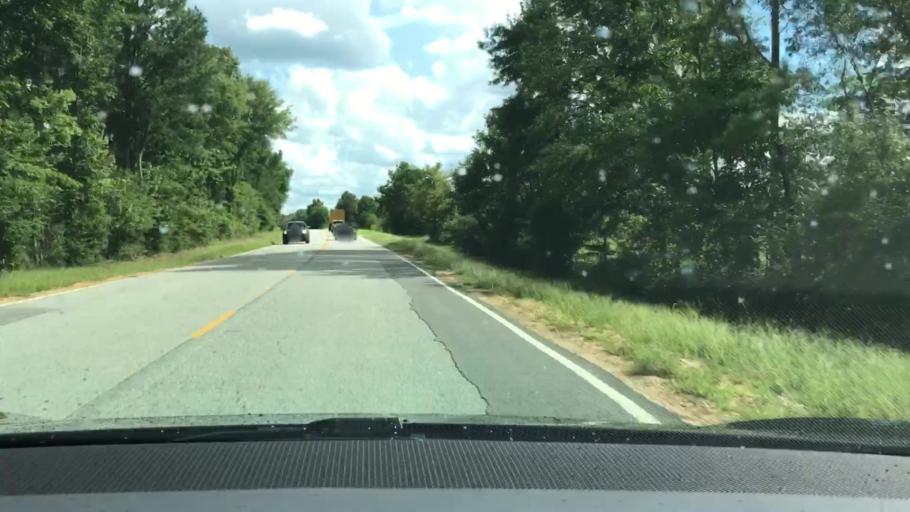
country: US
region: Alabama
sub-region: Montgomery County
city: Pike Road
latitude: 32.2288
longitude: -86.0927
